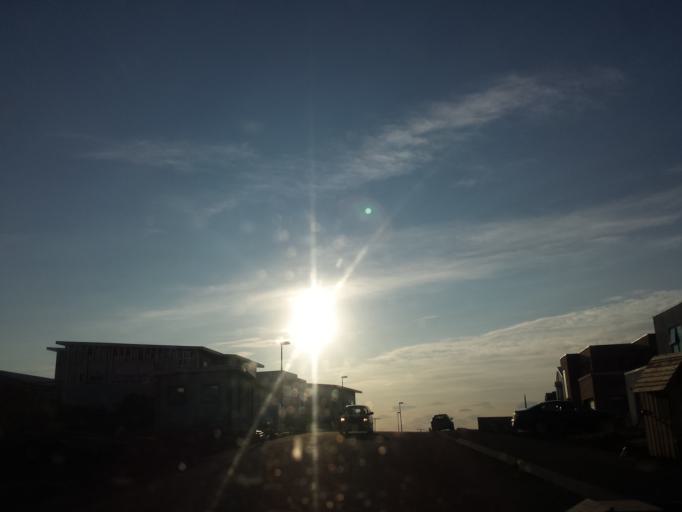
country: IS
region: Capital Region
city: Kopavogur
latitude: 64.0928
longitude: -21.8703
